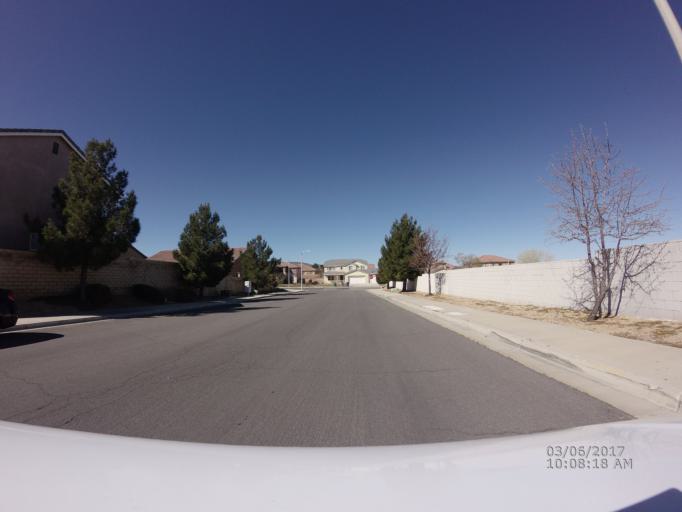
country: US
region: California
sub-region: Los Angeles County
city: Quartz Hill
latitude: 34.6517
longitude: -118.2050
